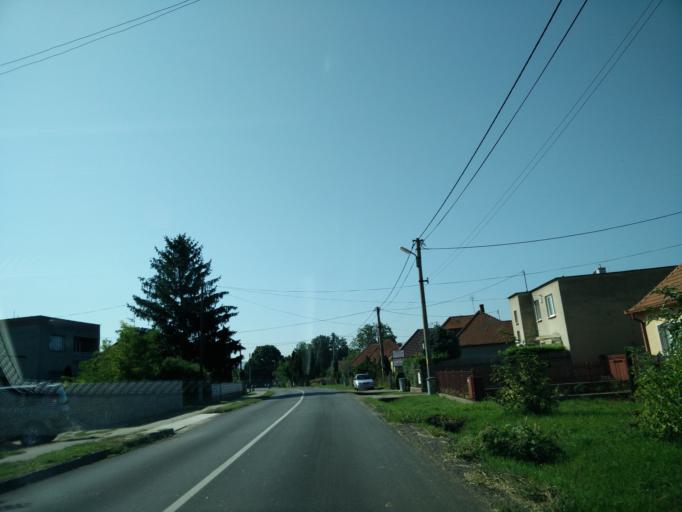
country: SK
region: Nitriansky
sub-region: Okres Nitra
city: Nitra
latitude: 48.4697
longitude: 18.1432
